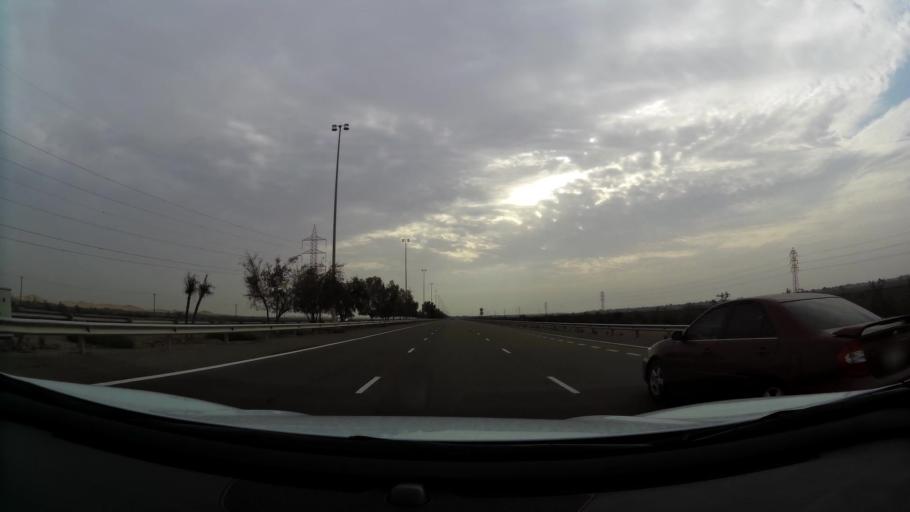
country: AE
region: Abu Dhabi
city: Abu Dhabi
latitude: 24.2170
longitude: 54.8673
